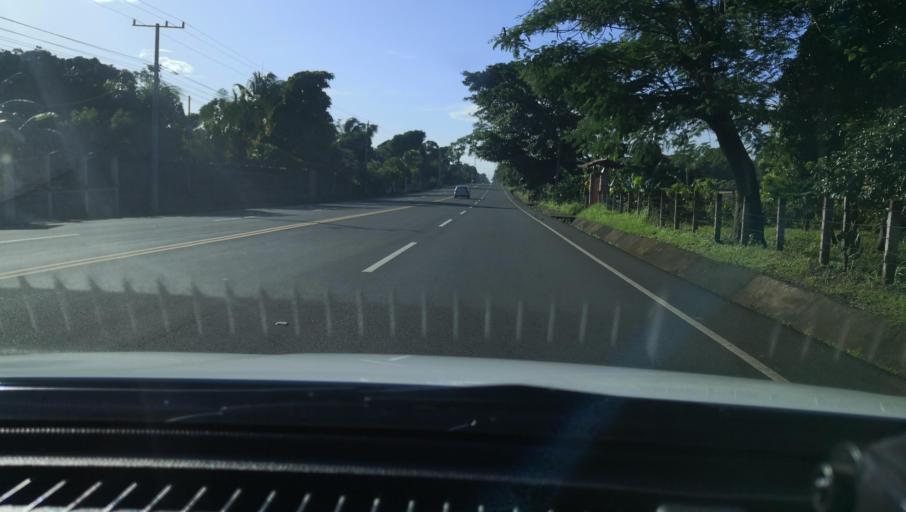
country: NI
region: Carazo
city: La Paz de Oriente
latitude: 11.8173
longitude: -86.1435
